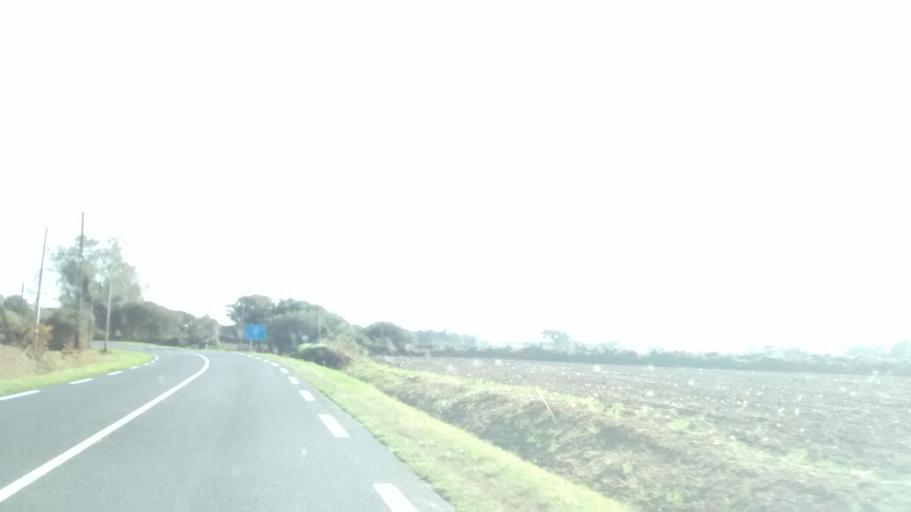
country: FR
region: Brittany
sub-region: Departement des Cotes-d'Armor
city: Pleumeur-Bodou
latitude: 48.7557
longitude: -3.5259
